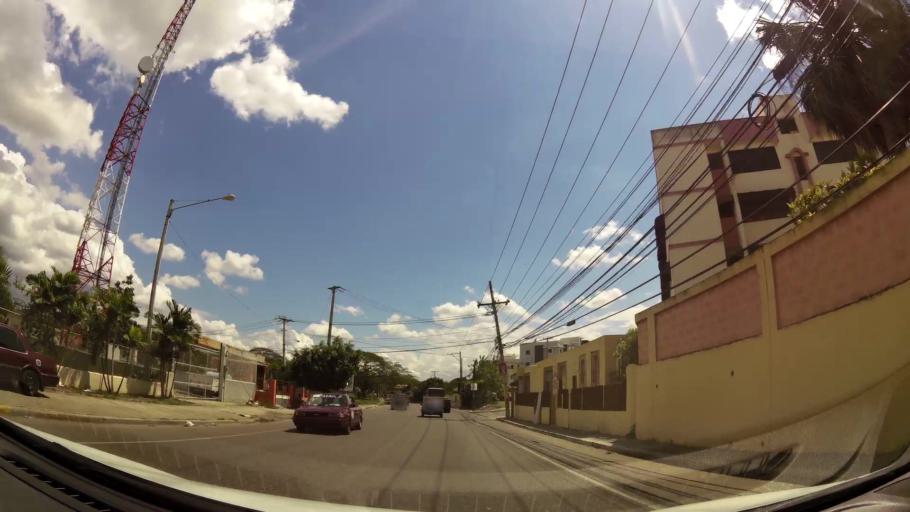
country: DO
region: Santiago
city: Santiago de los Caballeros
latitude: 19.4235
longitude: -70.6833
